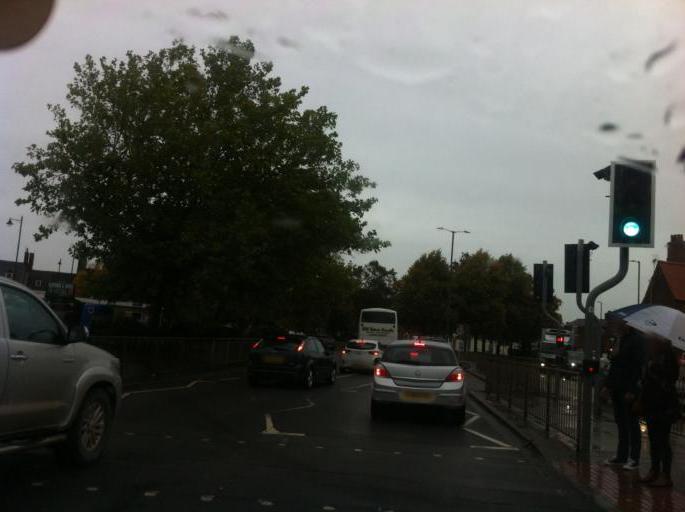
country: GB
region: England
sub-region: Lincolnshire
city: Boston
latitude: 52.9805
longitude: -0.0186
